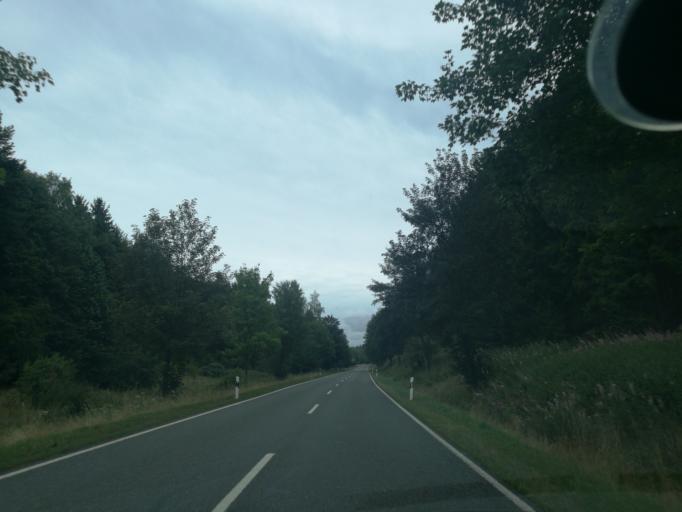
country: DE
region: Bavaria
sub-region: Upper Franconia
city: Regnitzlosau
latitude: 50.3116
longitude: 12.0372
